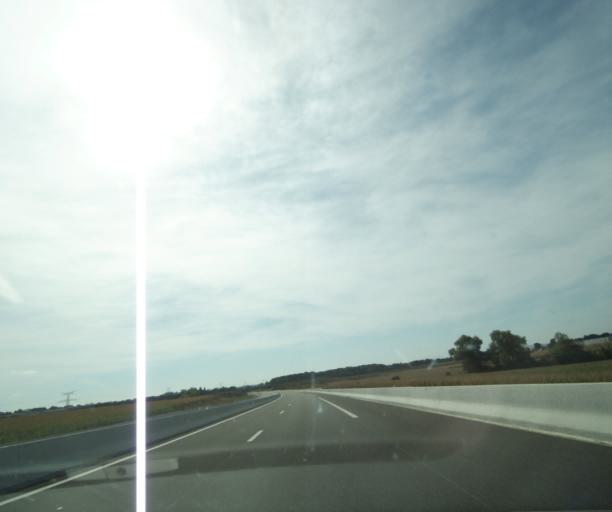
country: FR
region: Auvergne
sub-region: Departement de l'Allier
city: Vendat
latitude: 46.1319
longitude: 3.3003
